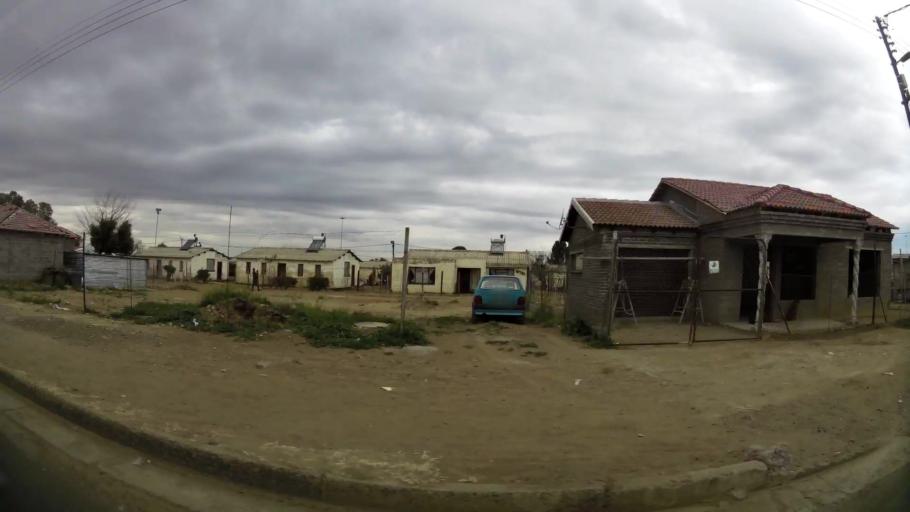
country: ZA
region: Orange Free State
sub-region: Fezile Dabi District Municipality
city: Kroonstad
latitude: -27.6531
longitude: 27.2105
